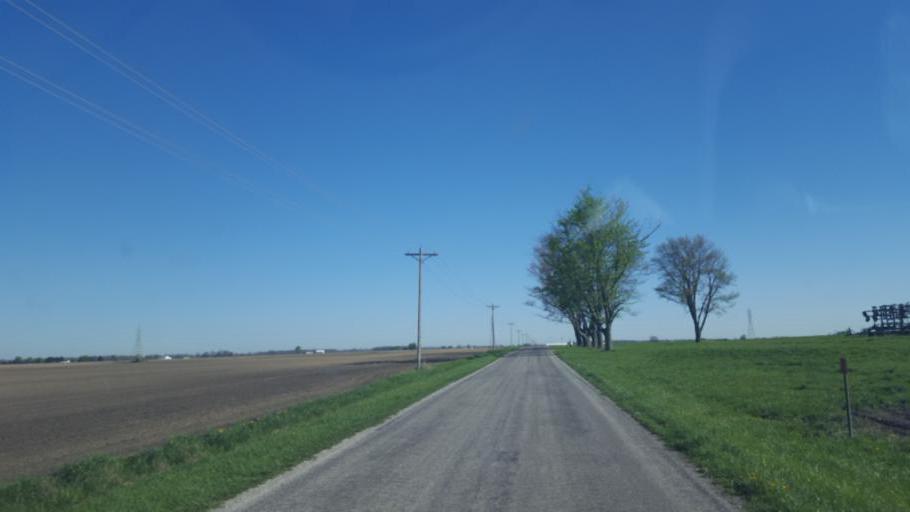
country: US
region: Ohio
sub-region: Marion County
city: Marion
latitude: 40.6759
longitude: -83.0685
